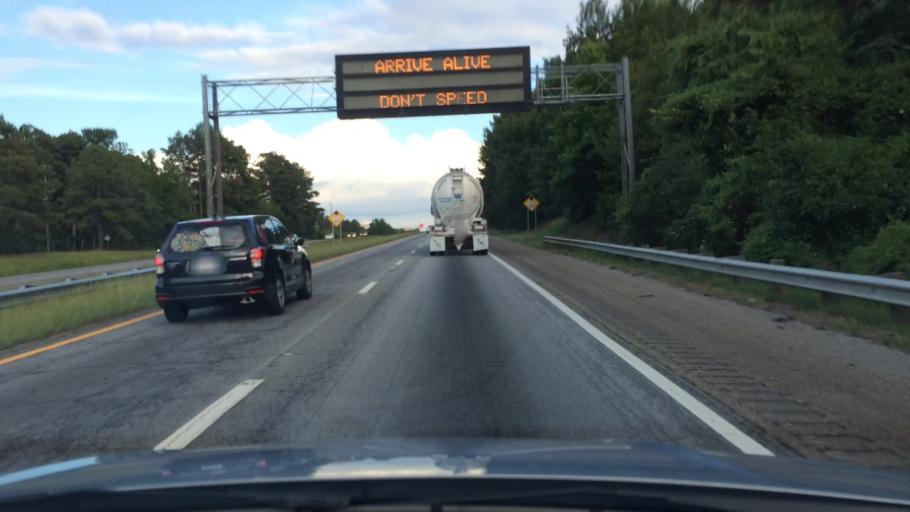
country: US
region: South Carolina
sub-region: Lexington County
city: Irmo
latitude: 34.1097
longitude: -81.1861
